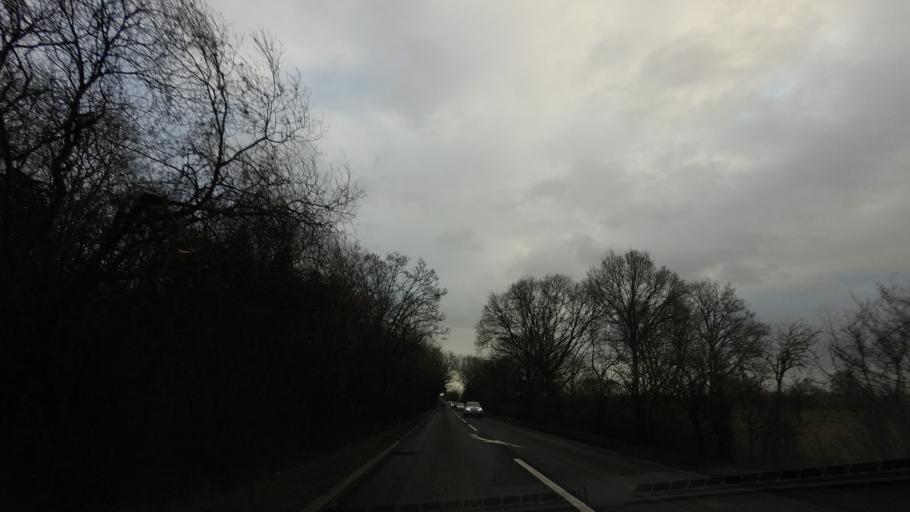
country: GB
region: England
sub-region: Kent
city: East Peckham
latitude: 51.2321
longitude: 0.3852
